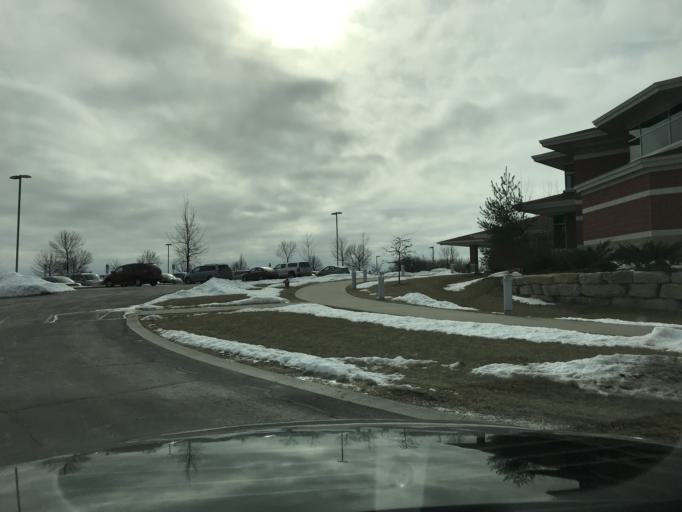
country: US
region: Wisconsin
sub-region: Dane County
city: Cottage Grove
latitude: 43.0925
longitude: -89.2644
